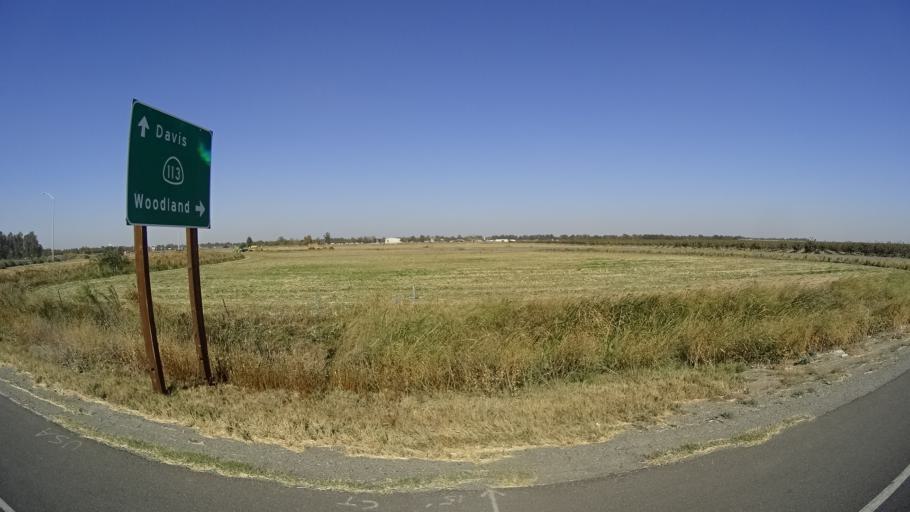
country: US
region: California
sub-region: Yolo County
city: Davis
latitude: 38.5902
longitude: -121.7643
